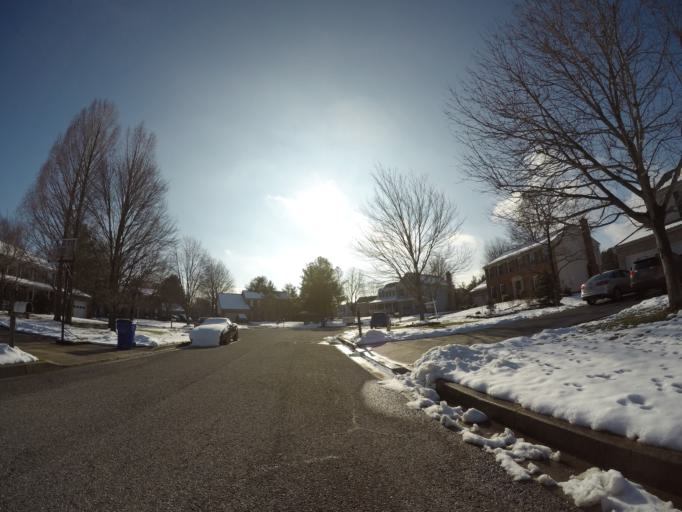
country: US
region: Maryland
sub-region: Howard County
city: Ilchester
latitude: 39.2158
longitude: -76.7844
